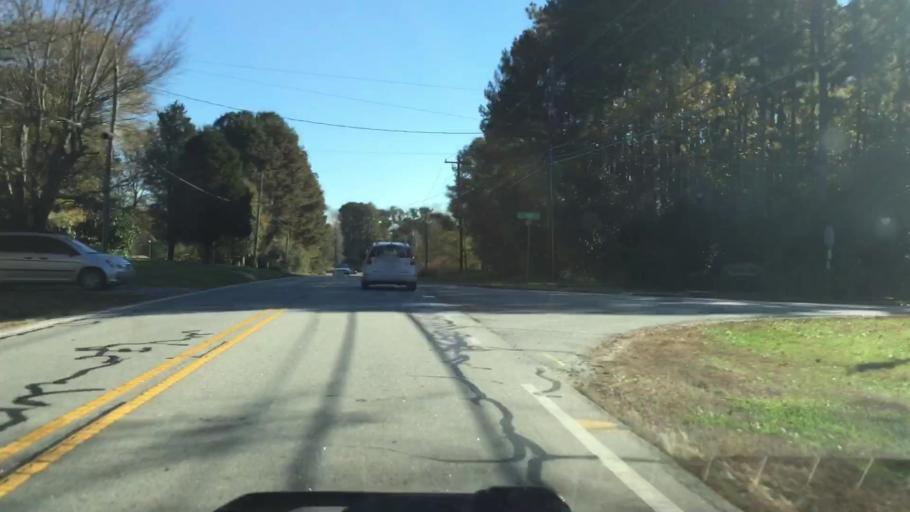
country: US
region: North Carolina
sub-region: Rowan County
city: Salisbury
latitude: 35.6613
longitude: -80.5523
